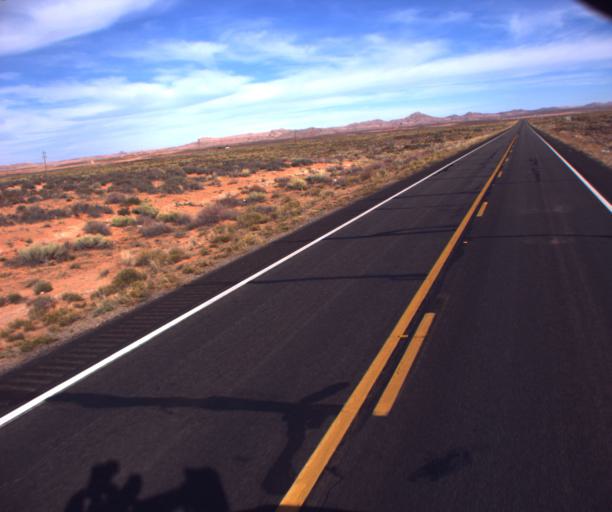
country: US
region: Arizona
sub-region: Apache County
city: Many Farms
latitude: 36.9401
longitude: -109.6746
